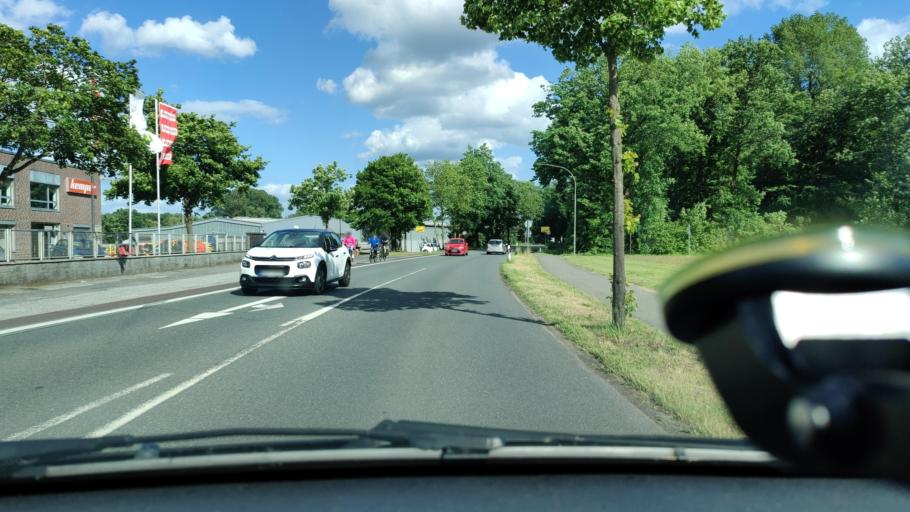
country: DE
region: North Rhine-Westphalia
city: Stadtlohn
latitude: 51.9915
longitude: 6.9320
